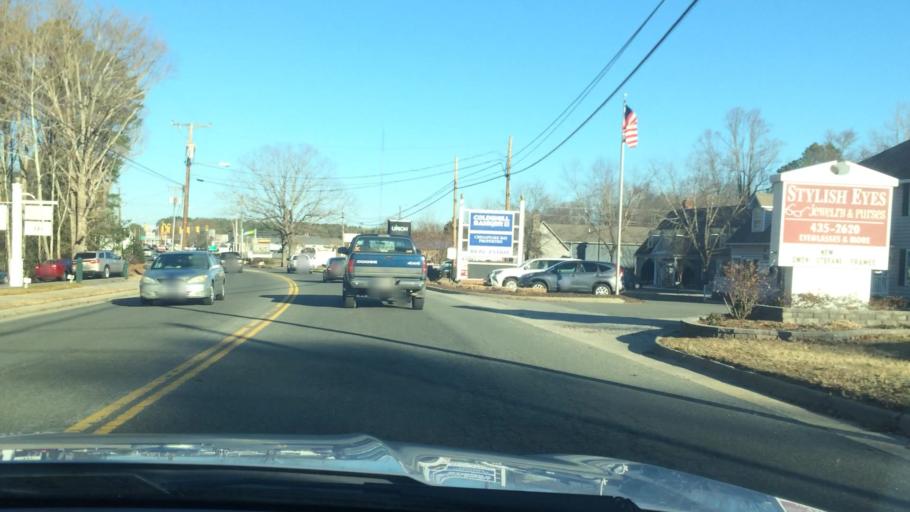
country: US
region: Virginia
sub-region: Lancaster County
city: Kilmarnock
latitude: 37.7164
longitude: -76.3816
